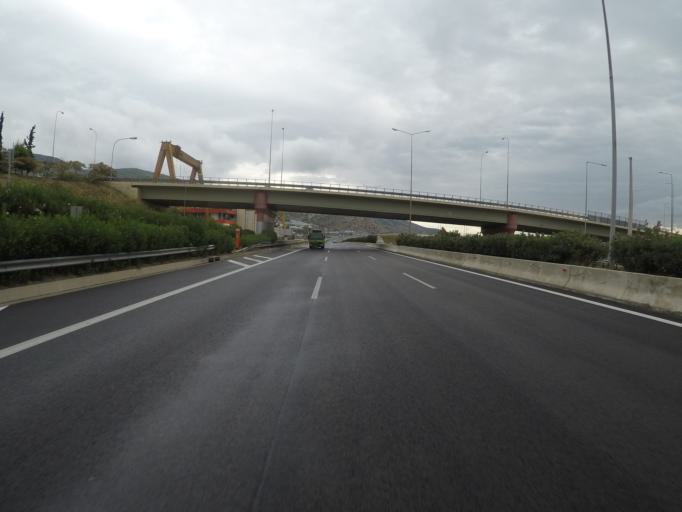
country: GR
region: Attica
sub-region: Nomarchia Dytikis Attikis
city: Vlychada
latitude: 38.0204
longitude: 23.4284
